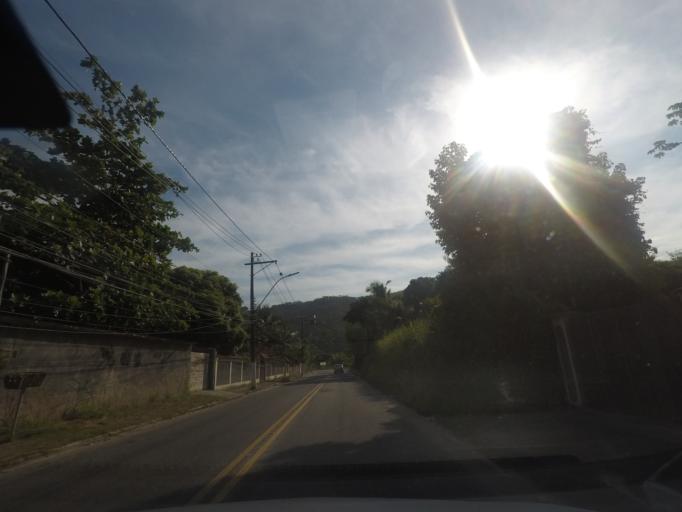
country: BR
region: Rio de Janeiro
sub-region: Niteroi
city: Niteroi
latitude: -22.9639
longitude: -43.0152
